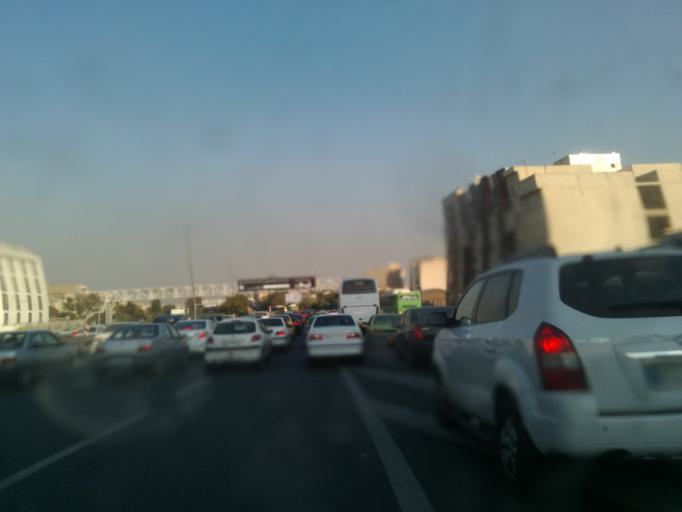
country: IR
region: Tehran
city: Tehran
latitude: 35.7117
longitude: 51.3396
